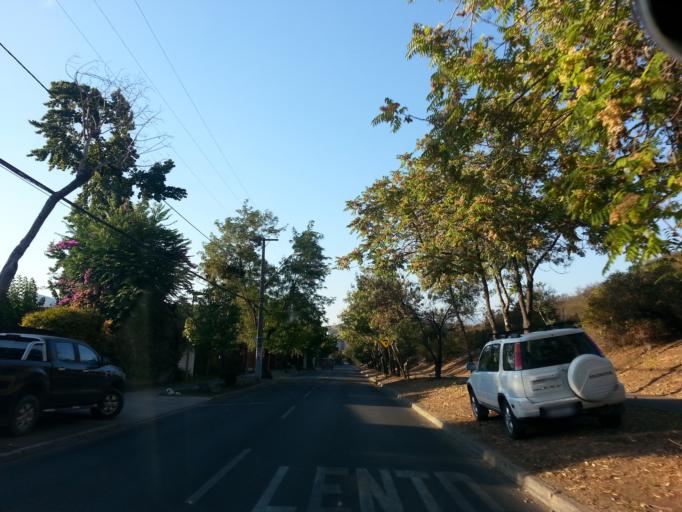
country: CL
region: Santiago Metropolitan
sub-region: Provincia de Santiago
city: Villa Presidente Frei, Nunoa, Santiago, Chile
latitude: -33.3977
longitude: -70.5400
